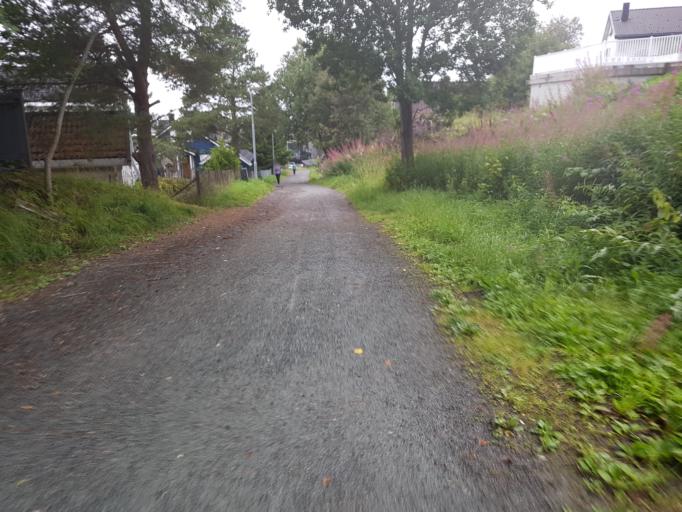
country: NO
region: Sor-Trondelag
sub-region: Trondheim
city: Trondheim
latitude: 63.4062
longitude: 10.4551
